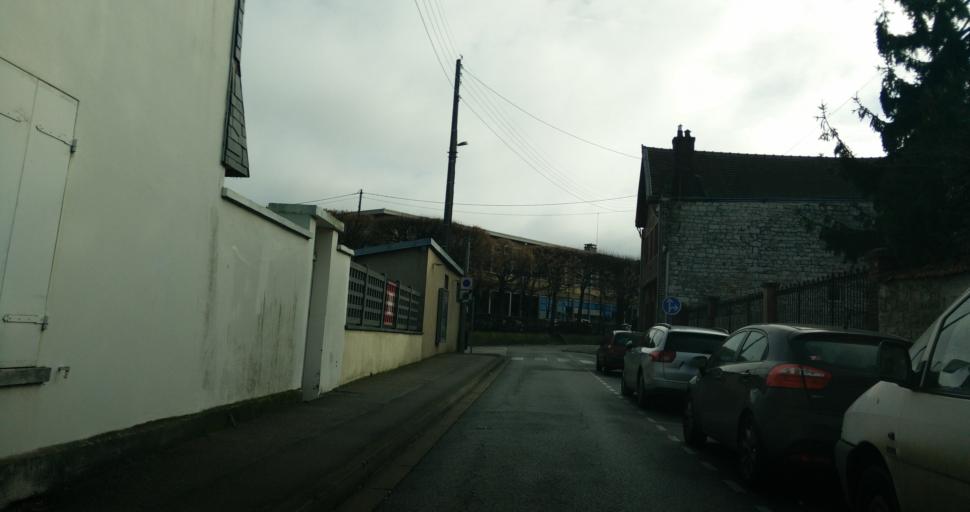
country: FR
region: Haute-Normandie
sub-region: Departement de l'Eure
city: Vernon
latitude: 49.0935
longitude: 1.4811
